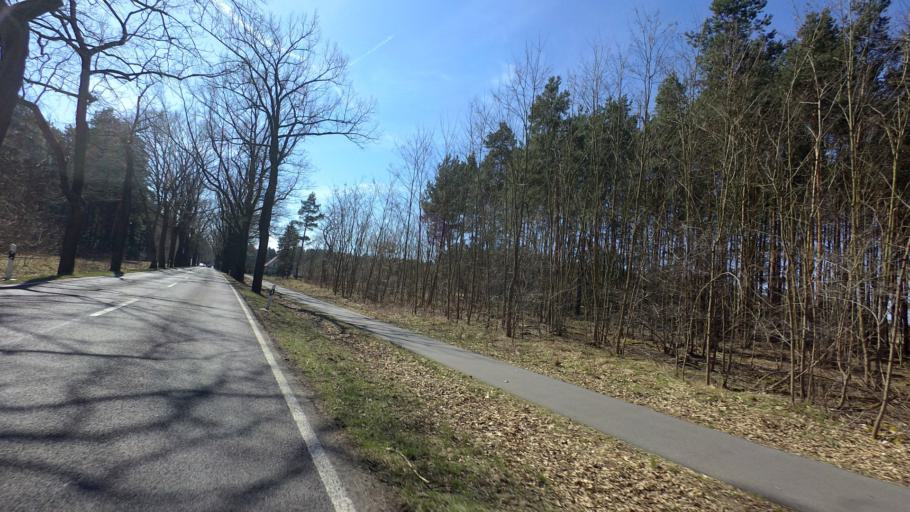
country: DE
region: Brandenburg
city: Schwerin
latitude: 52.1865
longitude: 13.5798
